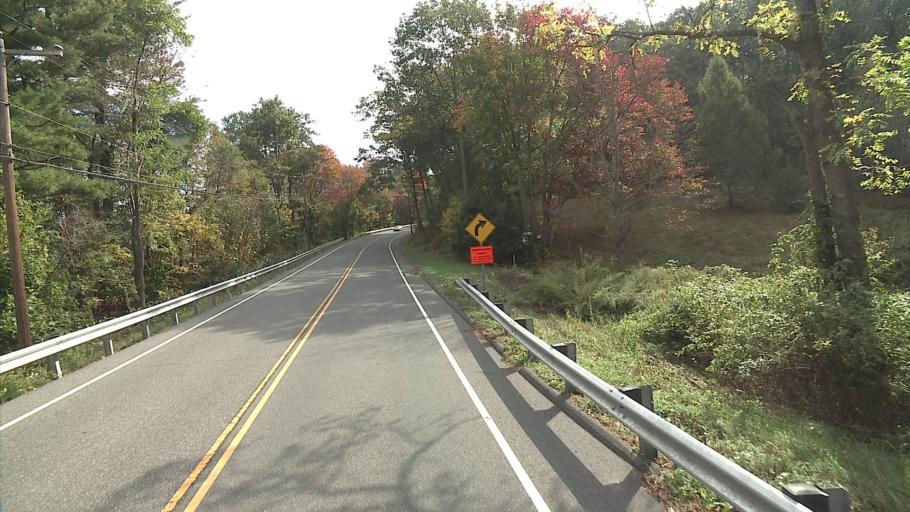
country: US
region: Connecticut
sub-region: Litchfield County
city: Watertown
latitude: 41.6006
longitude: -73.1569
